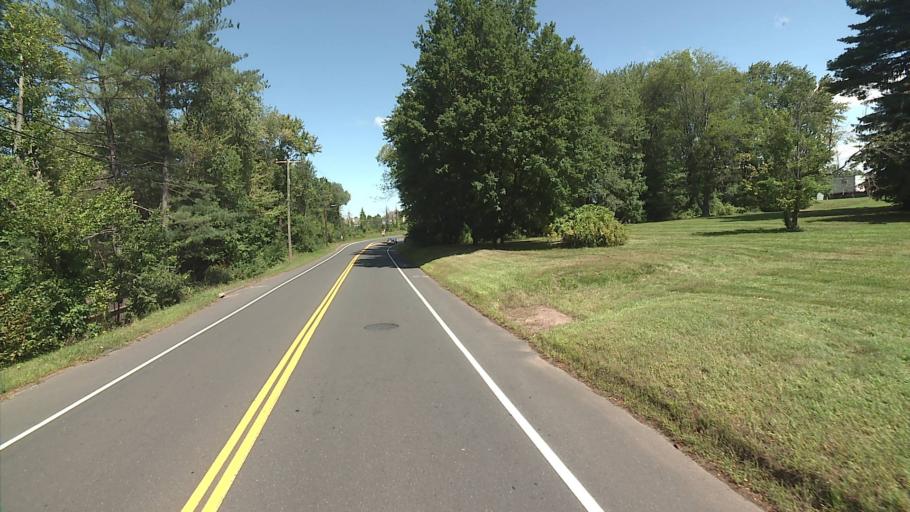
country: US
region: Connecticut
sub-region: Hartford County
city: Blue Hills
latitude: 41.8152
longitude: -72.7485
